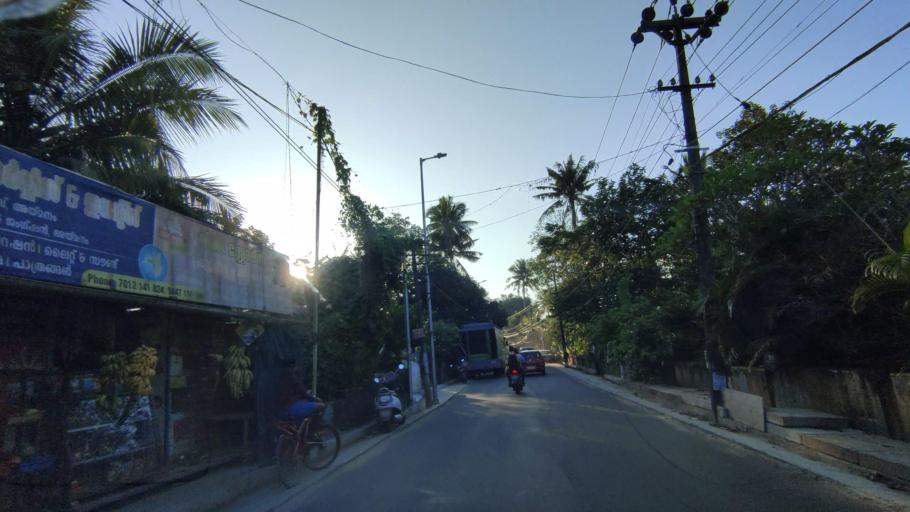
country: IN
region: Kerala
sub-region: Kottayam
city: Kottayam
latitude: 9.6116
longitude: 76.5019
